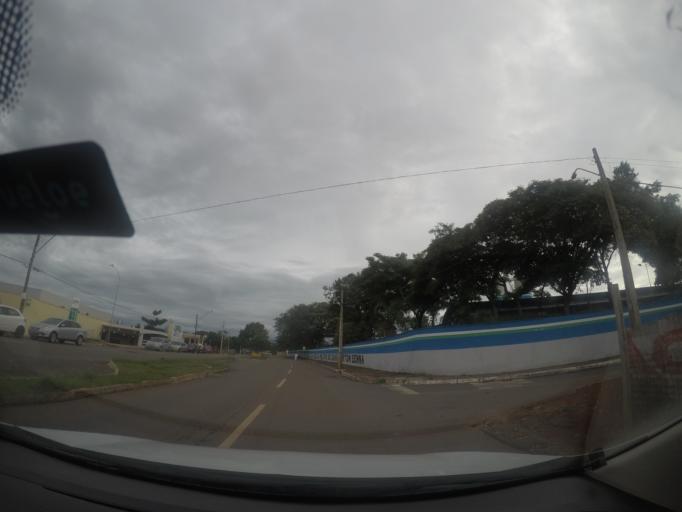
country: BR
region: Goias
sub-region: Goiania
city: Goiania
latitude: -16.6075
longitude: -49.3356
